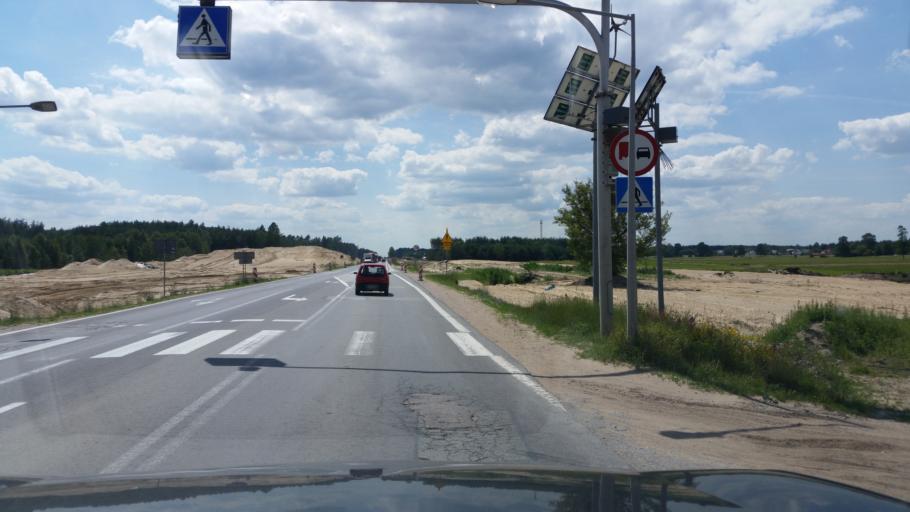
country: PL
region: Masovian Voivodeship
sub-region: Powiat ostrowski
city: Brok
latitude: 52.7572
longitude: 21.7955
